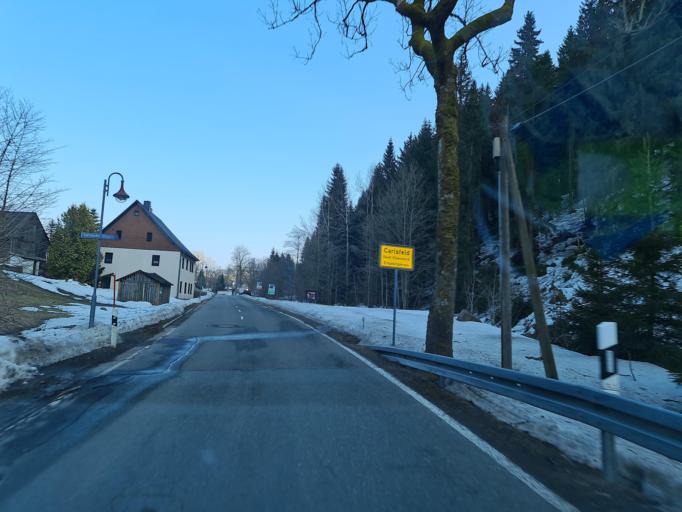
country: DE
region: Saxony
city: Eibenstock
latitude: 50.4385
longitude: 12.5776
